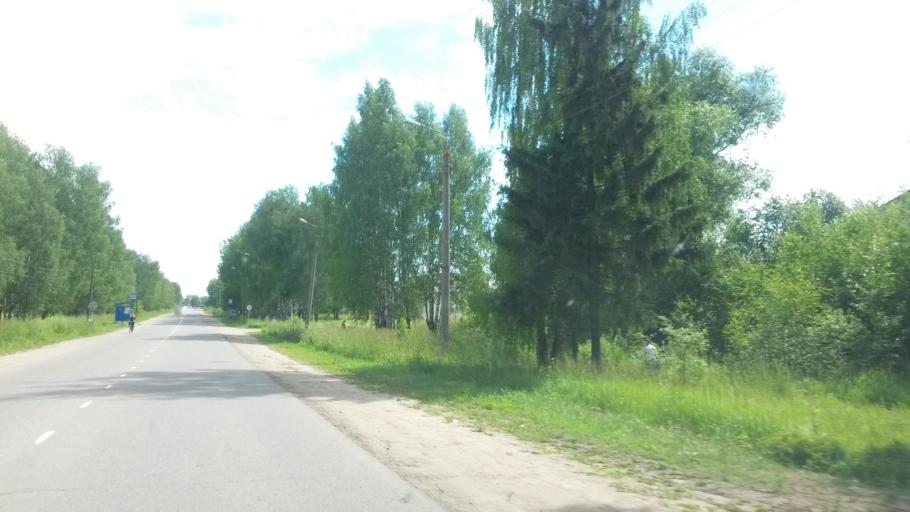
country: RU
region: Ivanovo
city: Zavolzhsk
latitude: 57.4725
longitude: 42.1571
